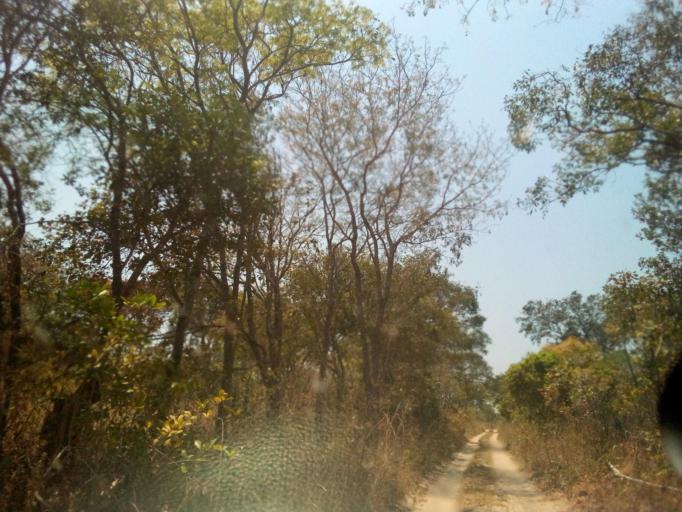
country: ZM
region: Copperbelt
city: Kataba
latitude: -12.2499
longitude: 30.3919
